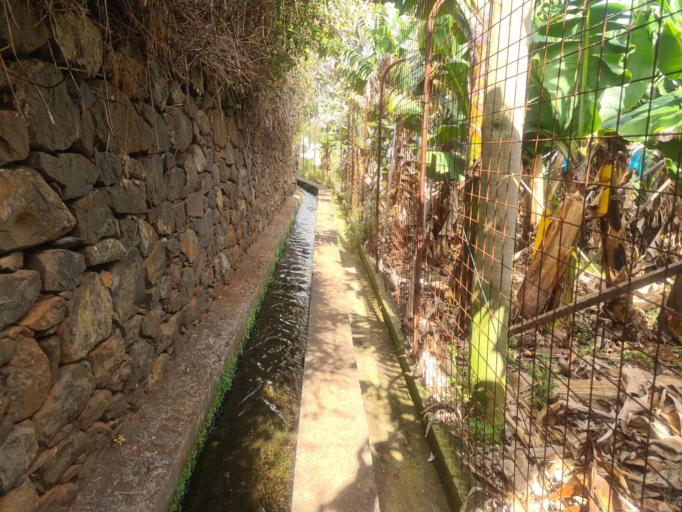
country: PT
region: Madeira
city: Camara de Lobos
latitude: 32.6551
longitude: -16.9481
